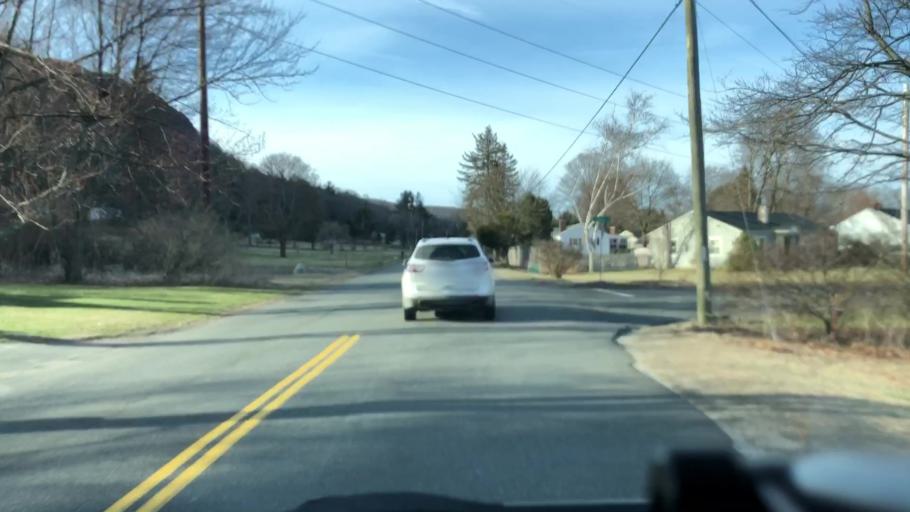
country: US
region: Massachusetts
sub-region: Hampshire County
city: Easthampton
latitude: 42.2559
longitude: -72.6523
